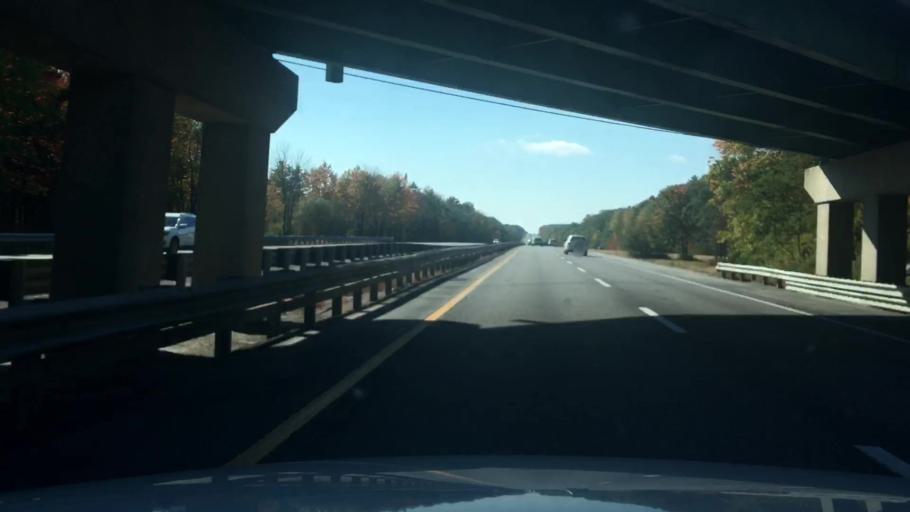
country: US
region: Maine
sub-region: Sagadahoc County
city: Topsham
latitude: 43.9149
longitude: -70.0293
